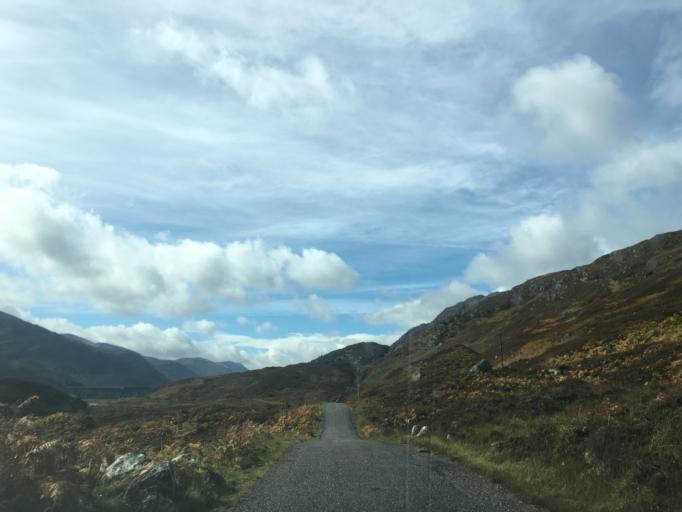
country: GB
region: Scotland
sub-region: Highland
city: Spean Bridge
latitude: 57.3480
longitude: -4.9177
